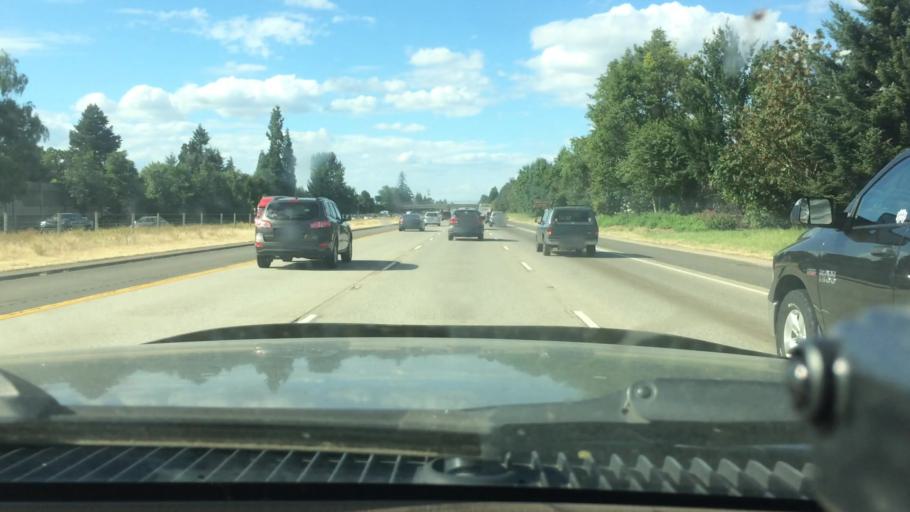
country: US
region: Oregon
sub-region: Marion County
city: Four Corners
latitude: 44.9347
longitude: -122.9902
